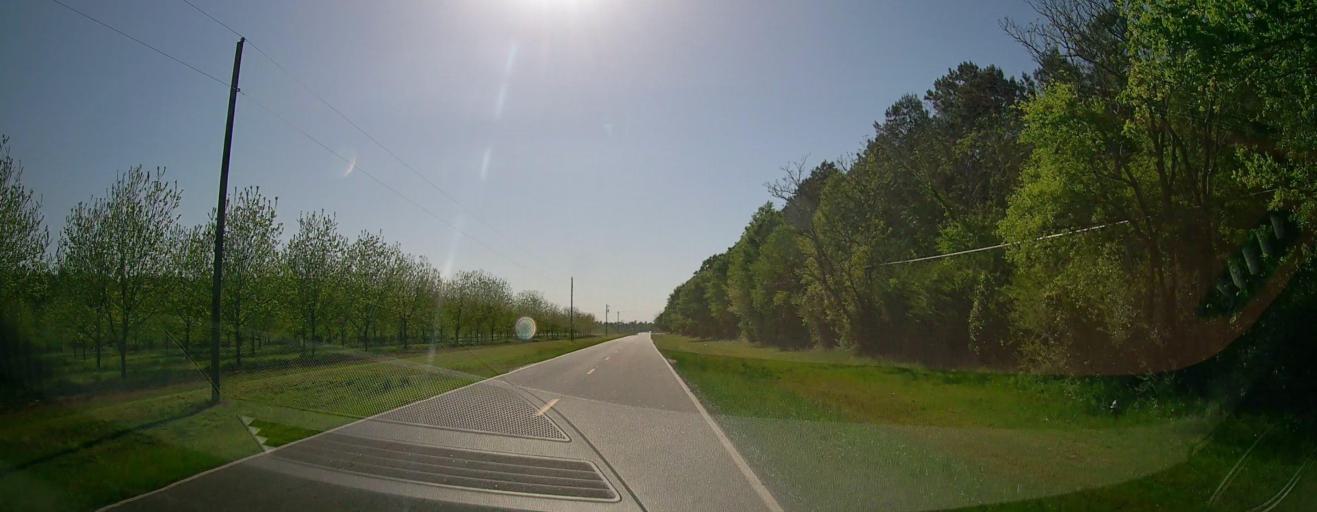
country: US
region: Georgia
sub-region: Houston County
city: Perry
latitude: 32.4516
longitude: -83.6493
